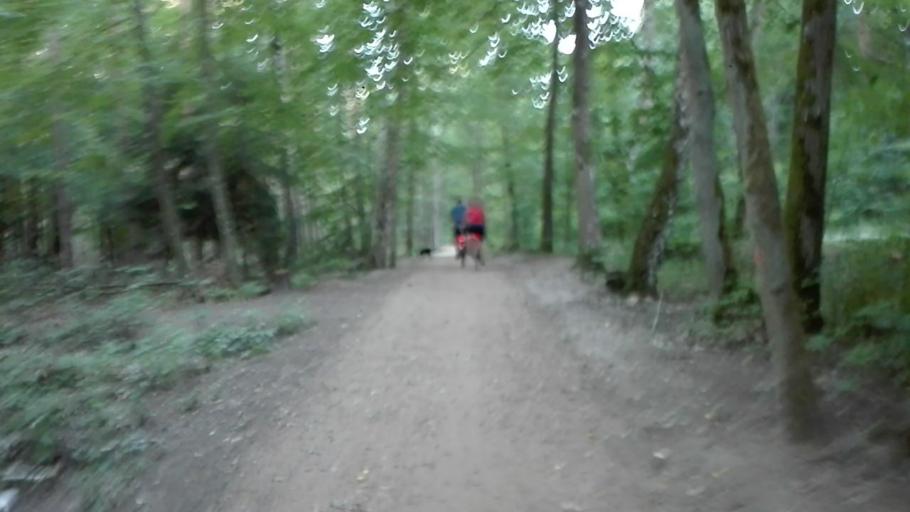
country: PL
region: West Pomeranian Voivodeship
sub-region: Powiat policki
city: Dobra
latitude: 53.4759
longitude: 14.3628
